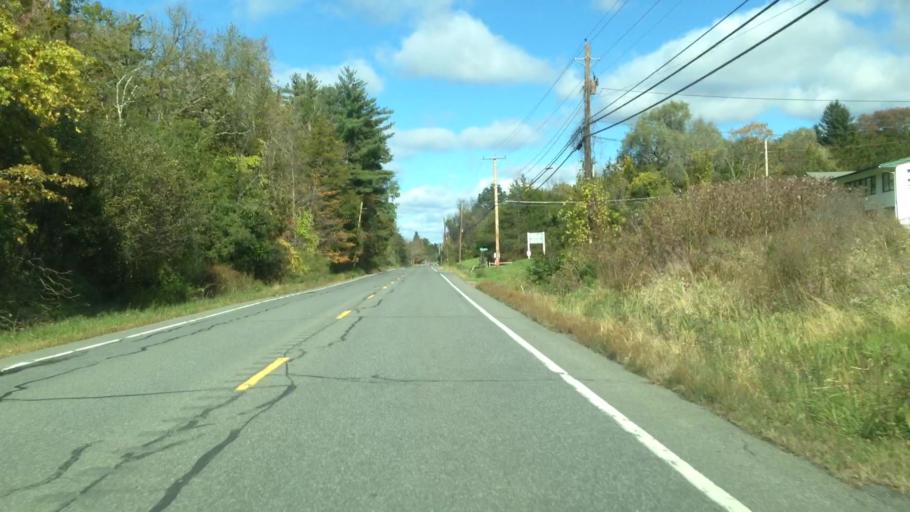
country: US
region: New York
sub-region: Ulster County
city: New Paltz
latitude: 41.7739
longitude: -74.0752
